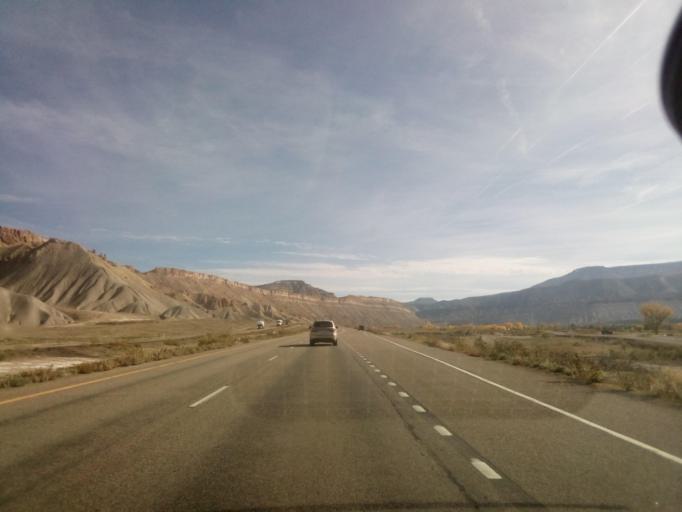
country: US
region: Colorado
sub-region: Mesa County
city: Clifton
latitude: 39.1113
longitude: -108.4148
